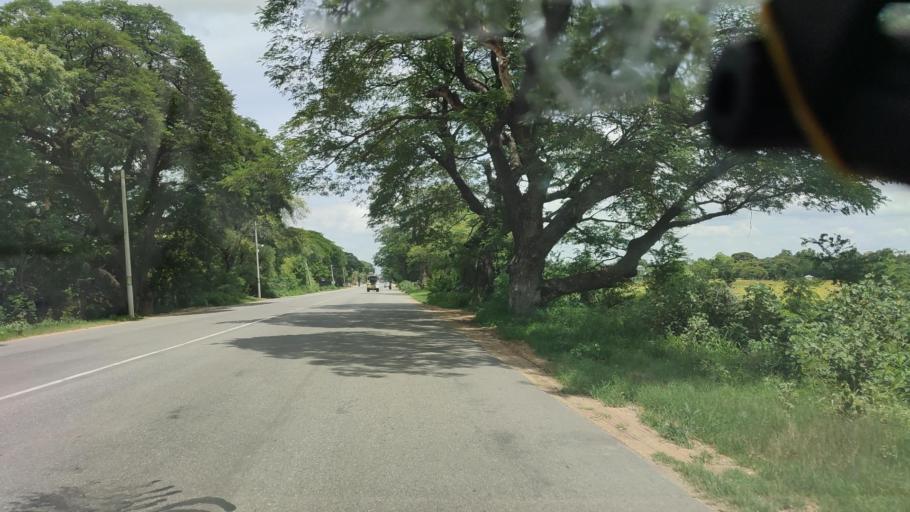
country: MM
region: Mandalay
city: Meiktila
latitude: 20.6722
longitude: 96.0019
